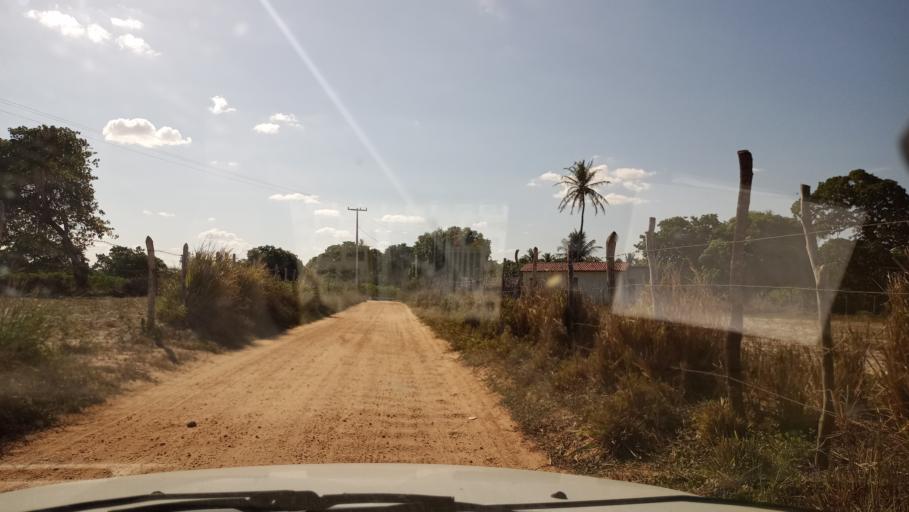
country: BR
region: Rio Grande do Norte
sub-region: Brejinho
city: Brejinho
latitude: -6.1760
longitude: -35.4622
